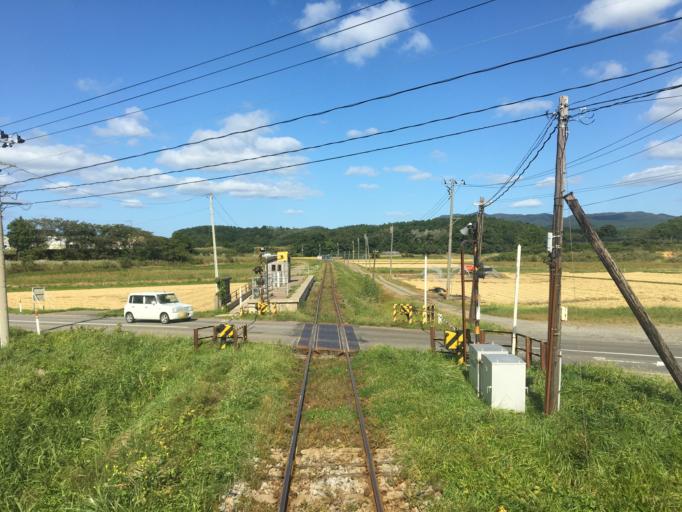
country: JP
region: Aomori
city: Goshogawara
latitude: 40.9506
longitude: 140.4404
